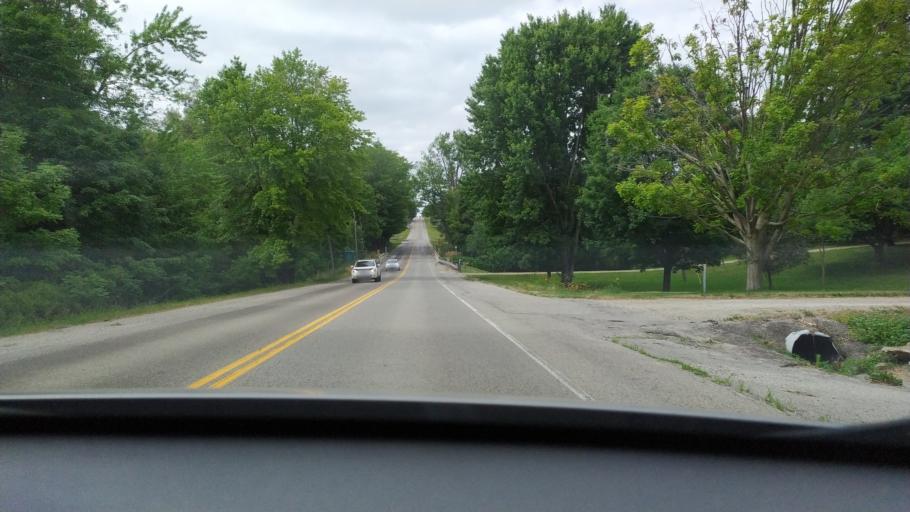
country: CA
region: Ontario
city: Stratford
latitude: 43.2949
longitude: -80.9725
